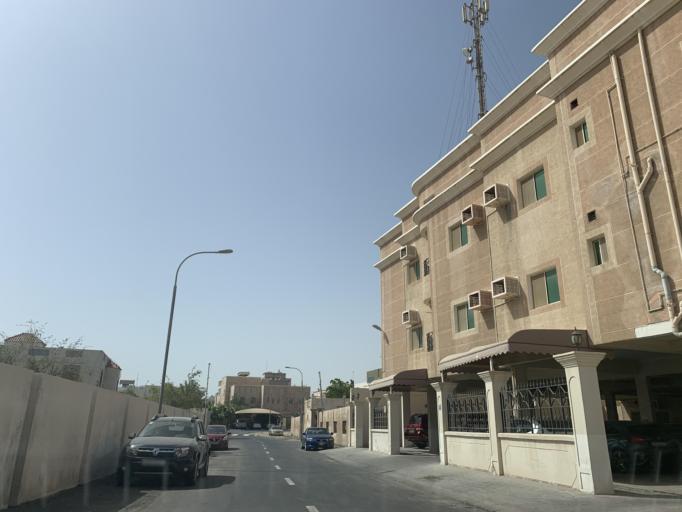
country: BH
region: Northern
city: Ar Rifa'
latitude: 26.1522
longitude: 50.5782
